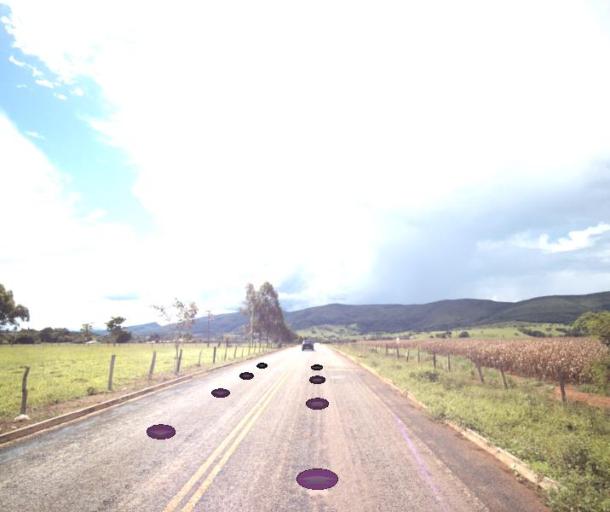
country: BR
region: Goias
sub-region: Pirenopolis
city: Pirenopolis
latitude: -16.0268
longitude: -49.1092
